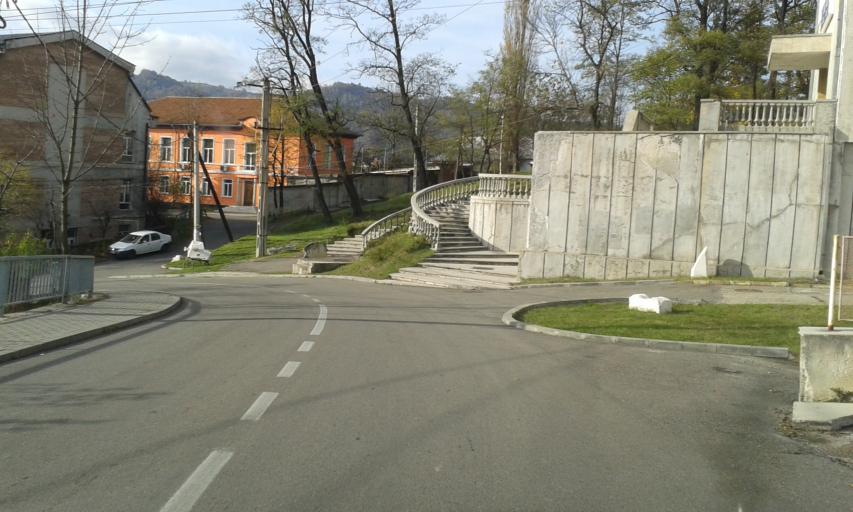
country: RO
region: Hunedoara
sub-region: Municipiul Petrosani
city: Petrosani
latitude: 45.4181
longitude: 23.3755
